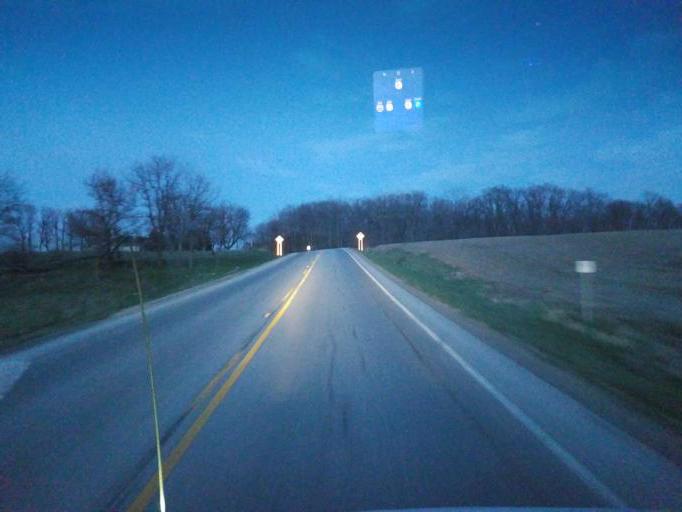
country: US
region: Ohio
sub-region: Logan County
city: De Graff
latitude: 40.3507
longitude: -83.9136
